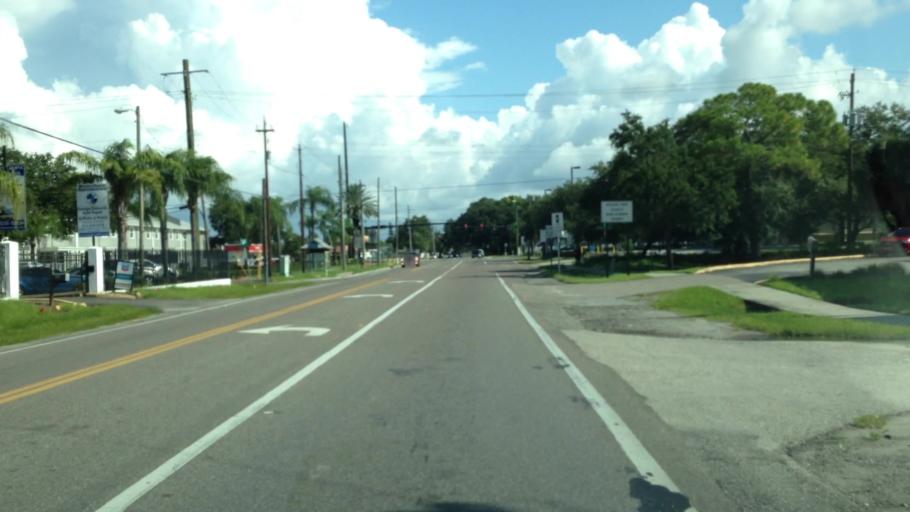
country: US
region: Florida
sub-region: Hillsborough County
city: Tampa
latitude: 27.8918
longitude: -82.5268
